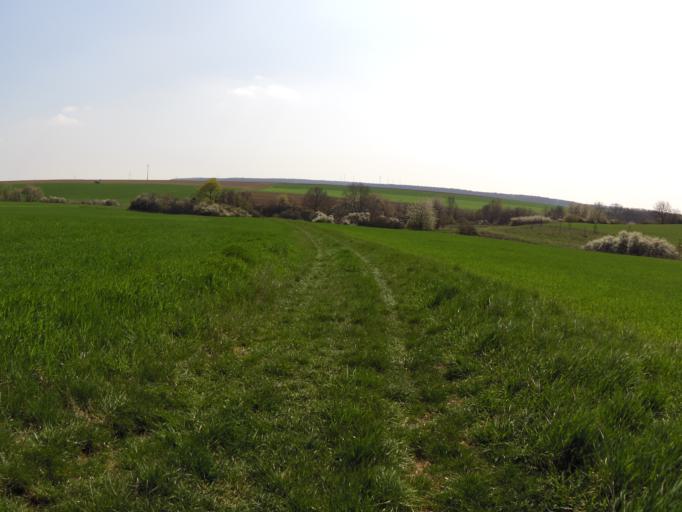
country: DE
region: Bavaria
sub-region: Regierungsbezirk Unterfranken
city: Gerbrunn
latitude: 49.7651
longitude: 10.0099
